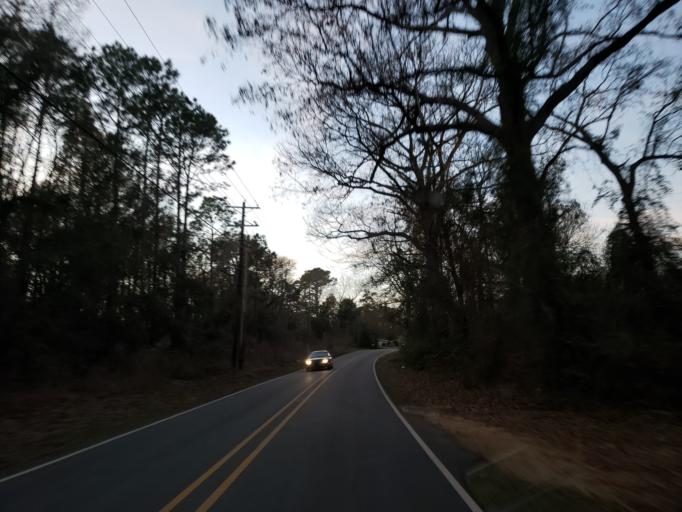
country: US
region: Mississippi
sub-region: Lamar County
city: West Hattiesburg
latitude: 31.2513
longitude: -89.3340
